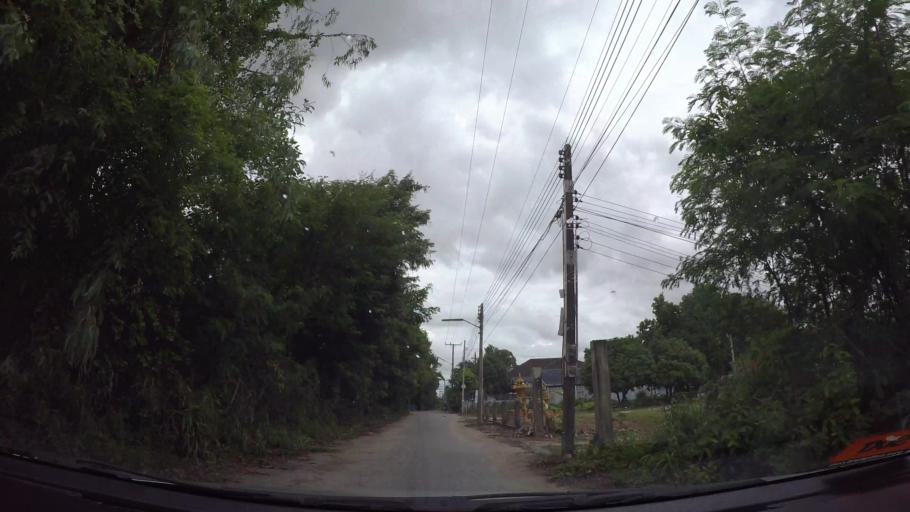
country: TH
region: Chon Buri
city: Si Racha
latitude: 13.1637
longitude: 100.9788
